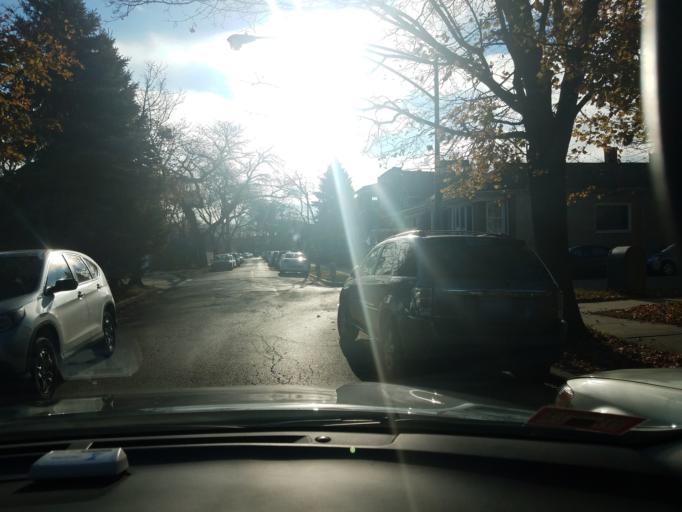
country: US
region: Illinois
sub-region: Cook County
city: Lincolnwood
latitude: 41.9632
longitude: -87.7313
